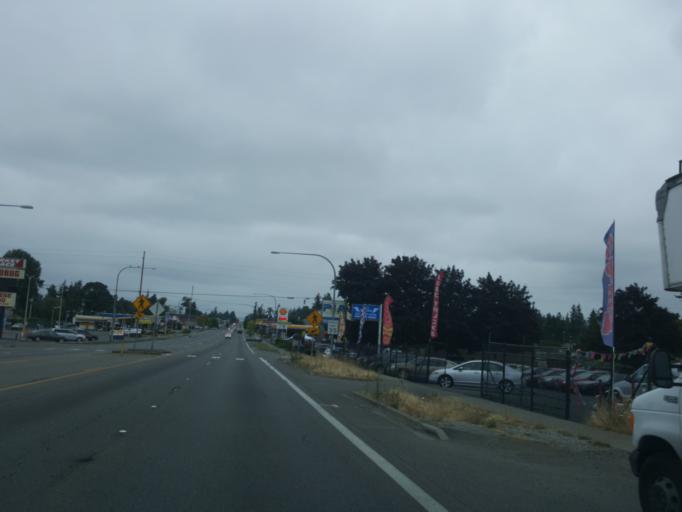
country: US
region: Washington
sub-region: Pierce County
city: Parkland
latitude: 47.1345
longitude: -122.4346
